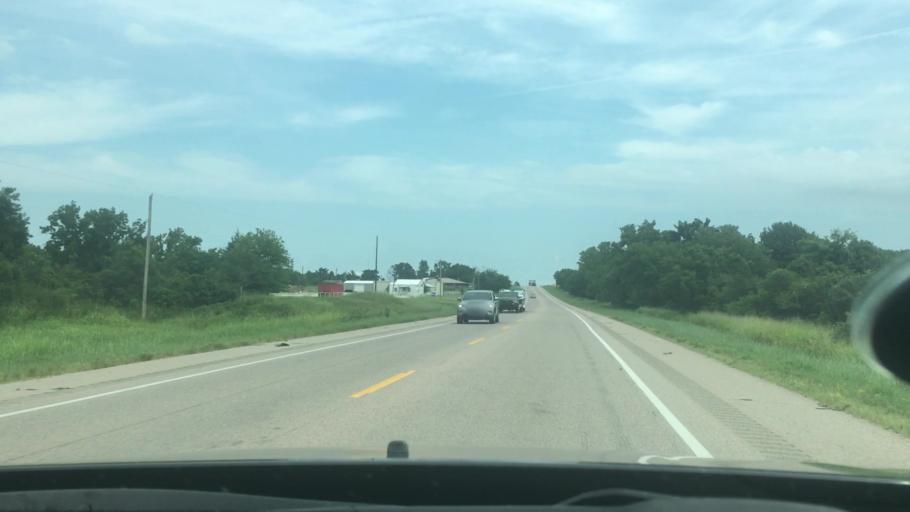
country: US
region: Oklahoma
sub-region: Seminole County
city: Seminole
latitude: 35.1765
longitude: -96.6741
